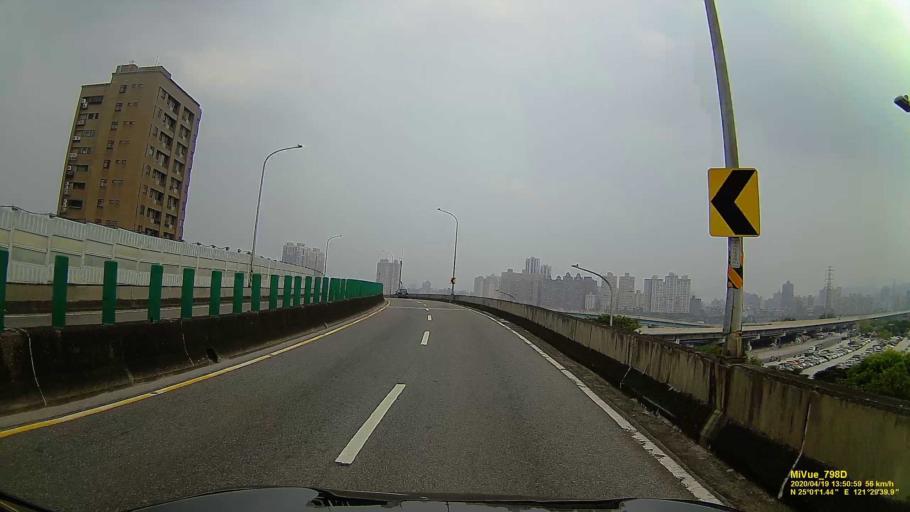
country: TW
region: Taipei
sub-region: Taipei
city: Banqiao
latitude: 25.0170
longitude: 121.4948
